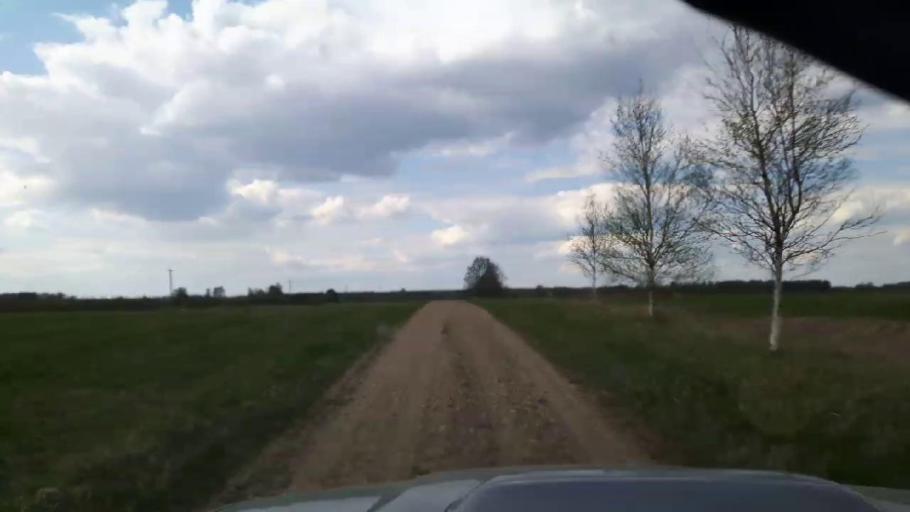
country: EE
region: Paernumaa
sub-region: Sindi linn
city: Sindi
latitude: 58.4327
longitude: 24.7508
